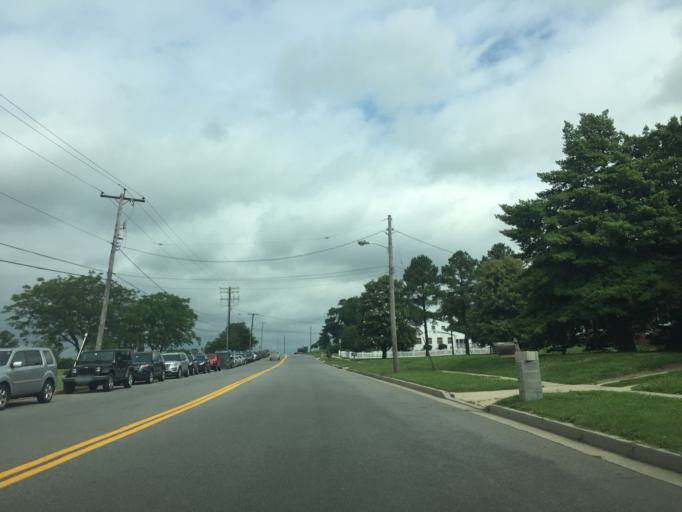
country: US
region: Maryland
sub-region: Baltimore County
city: Dundalk
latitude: 39.2621
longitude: -76.5135
